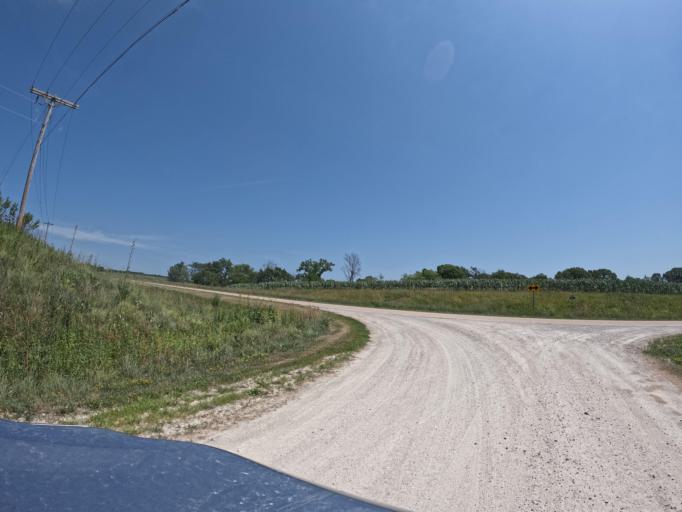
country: US
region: Iowa
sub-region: Henry County
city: Mount Pleasant
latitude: 40.9085
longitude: -91.5546
